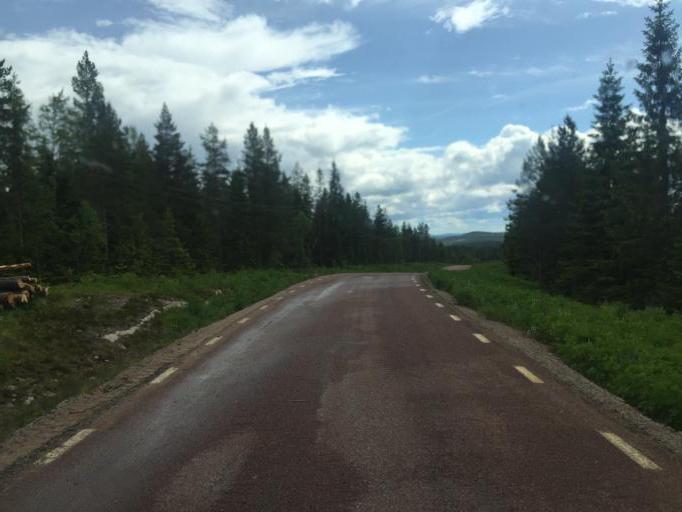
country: SE
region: Vaermland
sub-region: Hagfors Kommun
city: Hagfors
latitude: 60.3066
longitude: 13.8670
